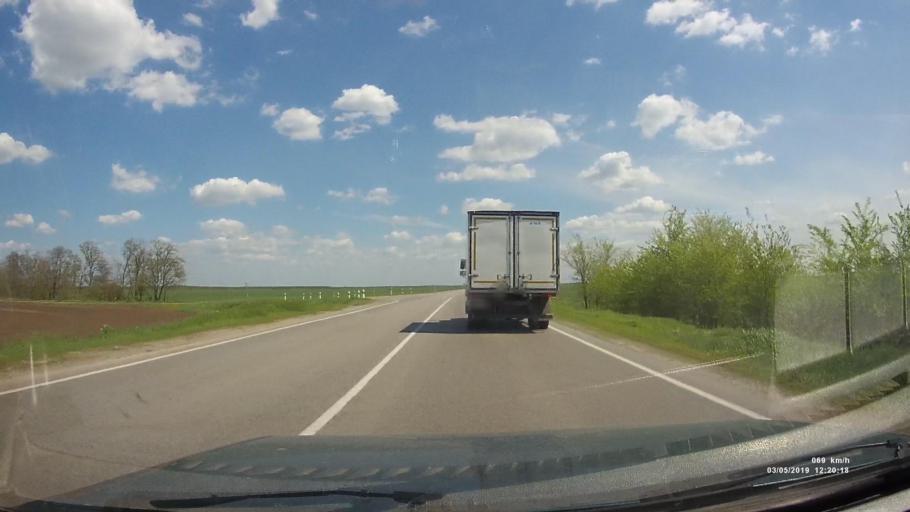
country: RU
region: Rostov
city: Melikhovskaya
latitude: 47.4044
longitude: 40.6198
